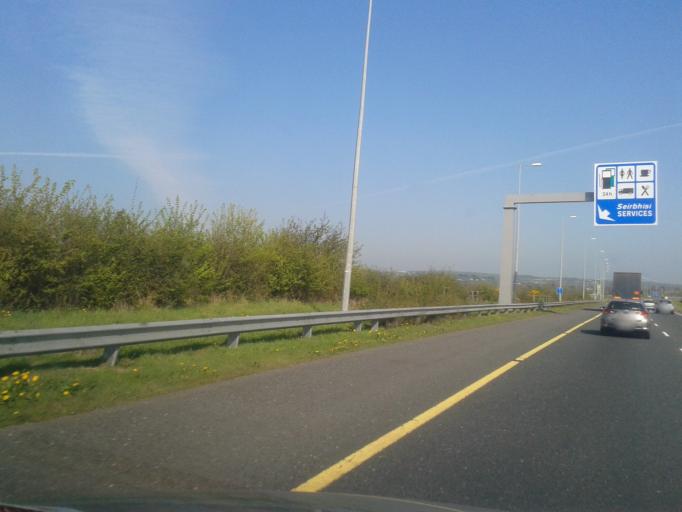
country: IE
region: Leinster
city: Lusk
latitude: 53.5337
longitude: -6.2089
